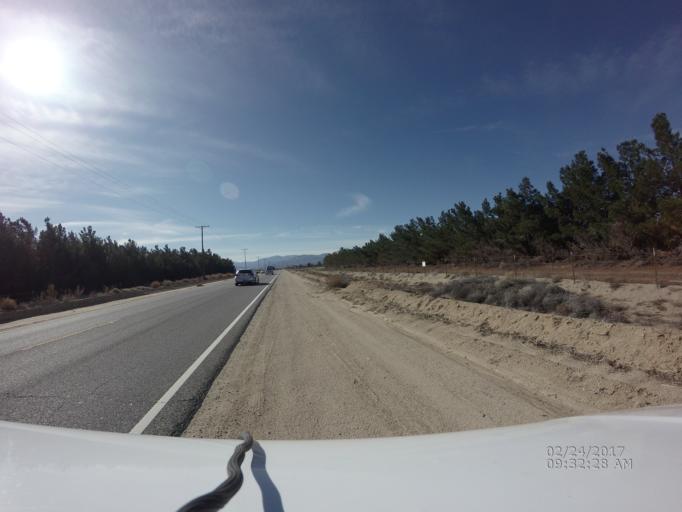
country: US
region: California
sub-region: Los Angeles County
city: Palmdale
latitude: 34.6129
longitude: -118.0410
